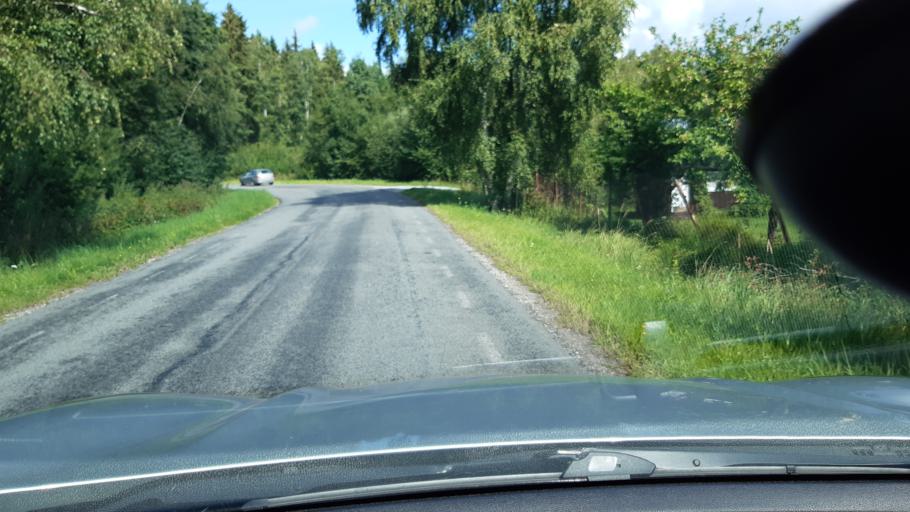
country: EE
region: Raplamaa
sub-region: Rapla vald
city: Rapla
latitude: 59.0115
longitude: 24.8130
